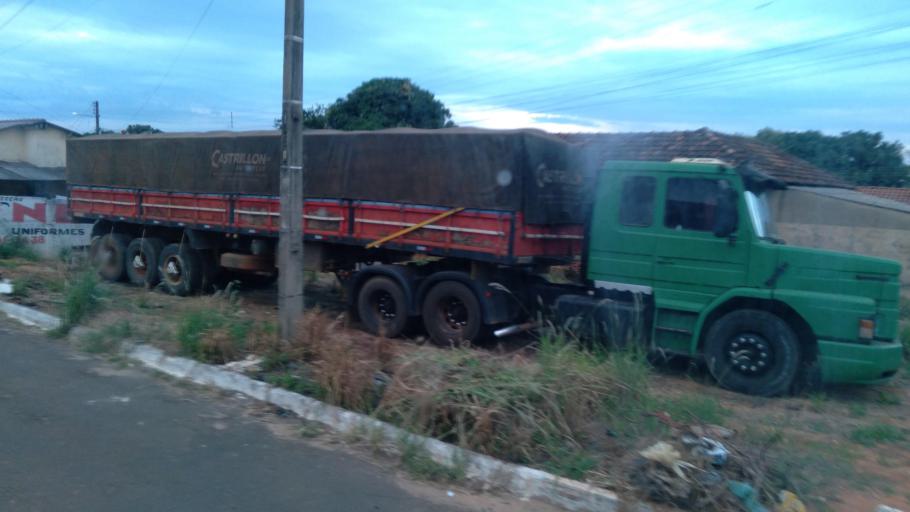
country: BR
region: Goias
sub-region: Mineiros
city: Mineiros
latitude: -17.5665
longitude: -52.5469
